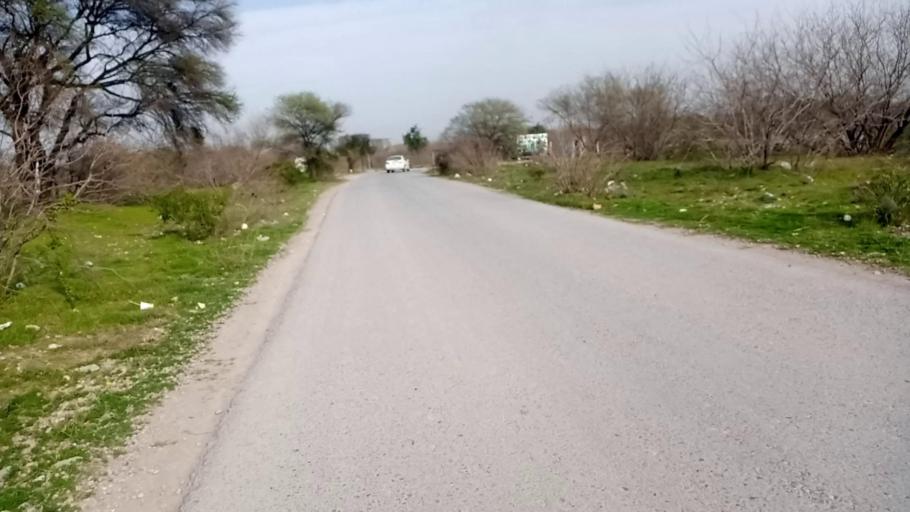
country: PK
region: Khyber Pakhtunkhwa
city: Peshawar
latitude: 34.0058
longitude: 71.4510
